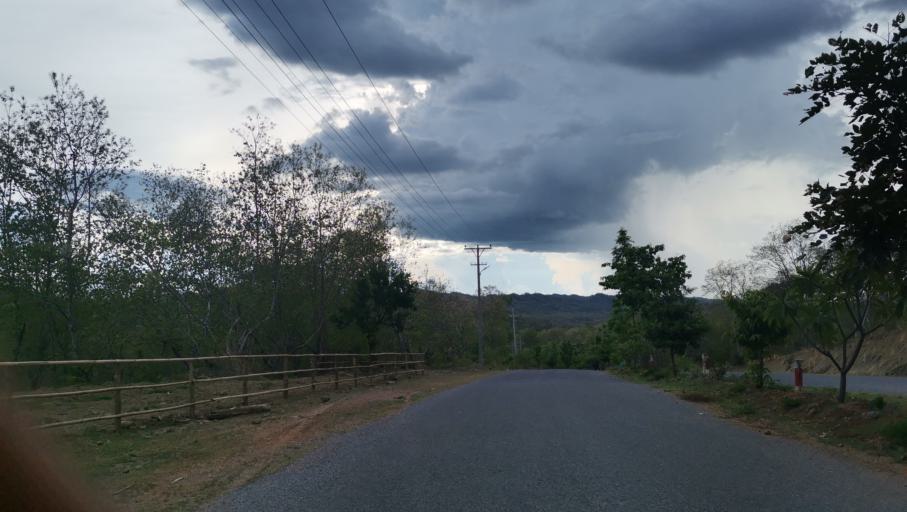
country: MM
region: Magway
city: Minbu
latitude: 20.1058
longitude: 94.5438
